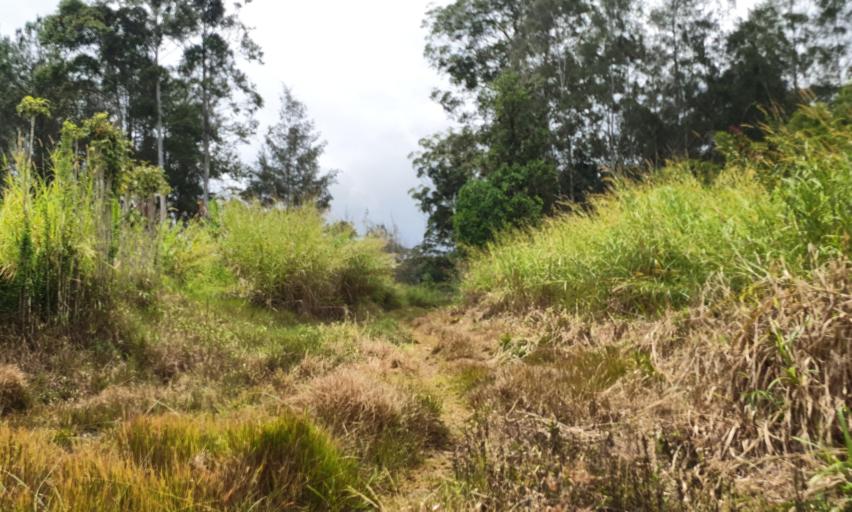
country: PG
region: Jiwaka
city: Minj
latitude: -5.9156
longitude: 144.8240
